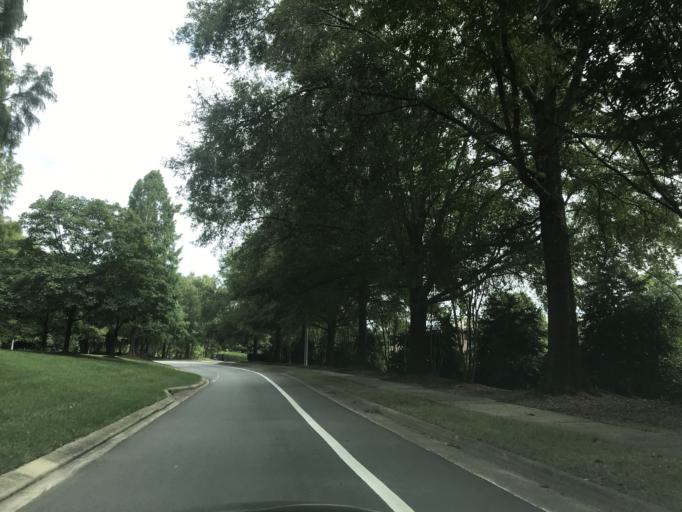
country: US
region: North Carolina
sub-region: Wake County
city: Cary
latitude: 35.7331
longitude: -78.7853
